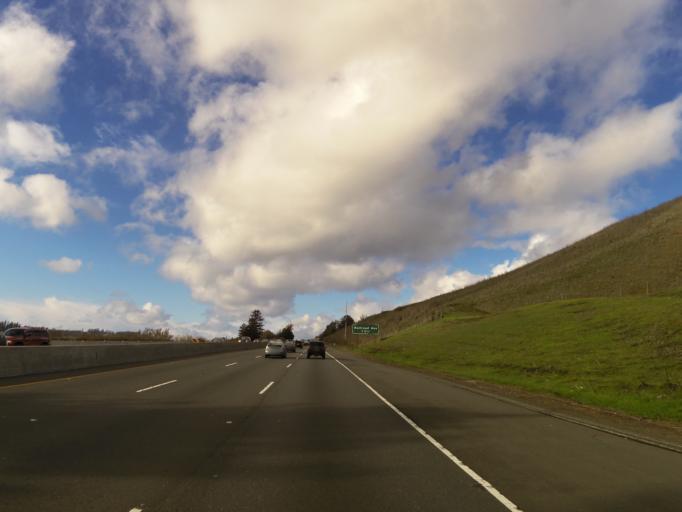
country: US
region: California
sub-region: Sonoma County
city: Penngrove
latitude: 38.2897
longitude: -122.6930
